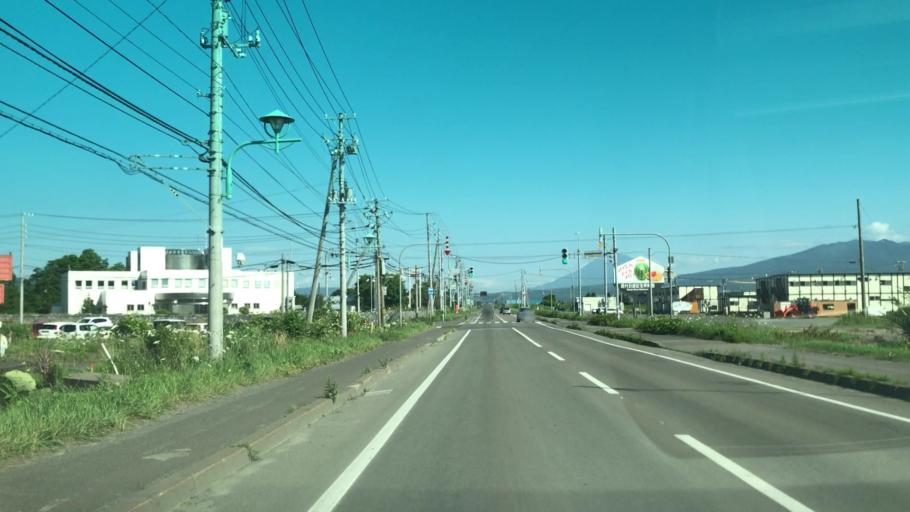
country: JP
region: Hokkaido
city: Iwanai
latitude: 43.0323
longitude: 140.5349
